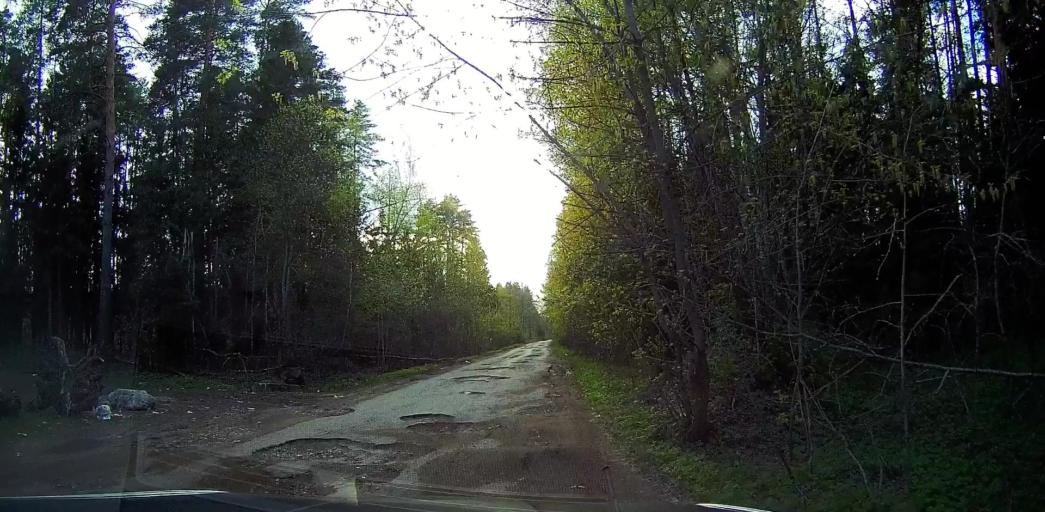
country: RU
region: Moskovskaya
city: Malyshevo
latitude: 55.5518
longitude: 38.3490
